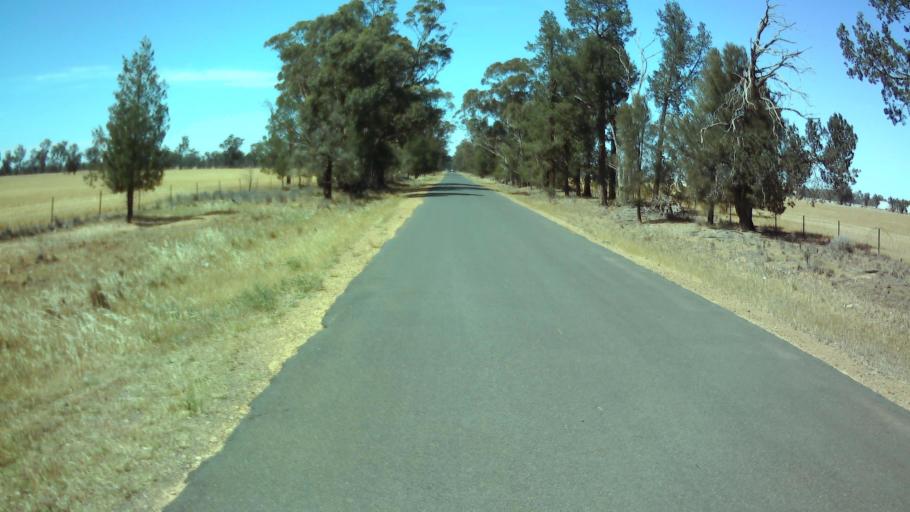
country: AU
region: New South Wales
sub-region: Weddin
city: Grenfell
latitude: -34.1084
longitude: 147.8862
